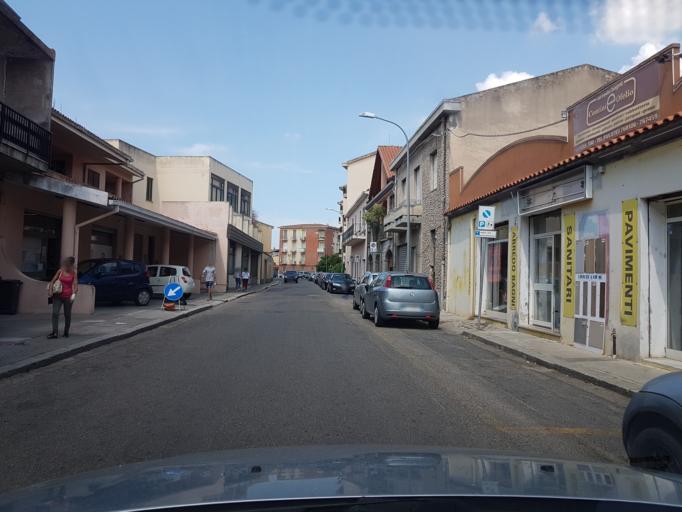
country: IT
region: Sardinia
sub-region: Provincia di Oristano
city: Oristano
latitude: 39.9070
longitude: 8.5958
